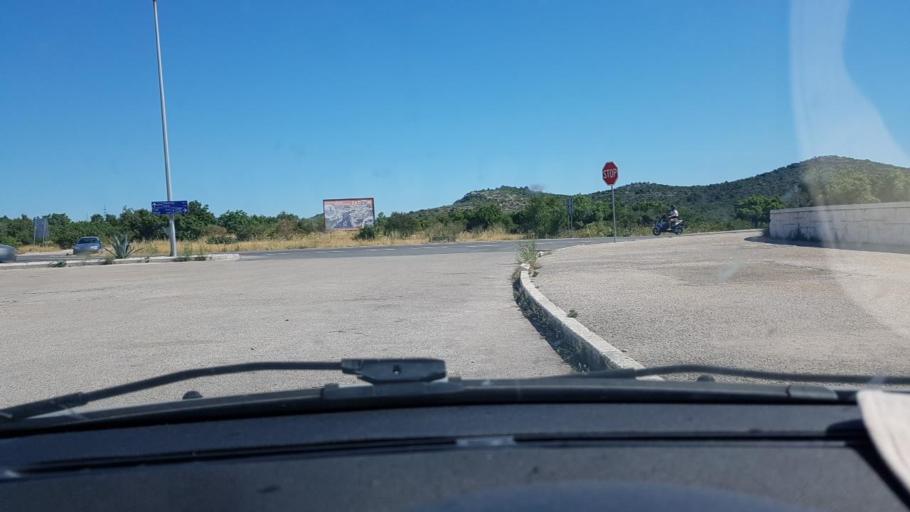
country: HR
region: Sibensko-Kniniska
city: Zaton
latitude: 43.7623
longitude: 15.8465
